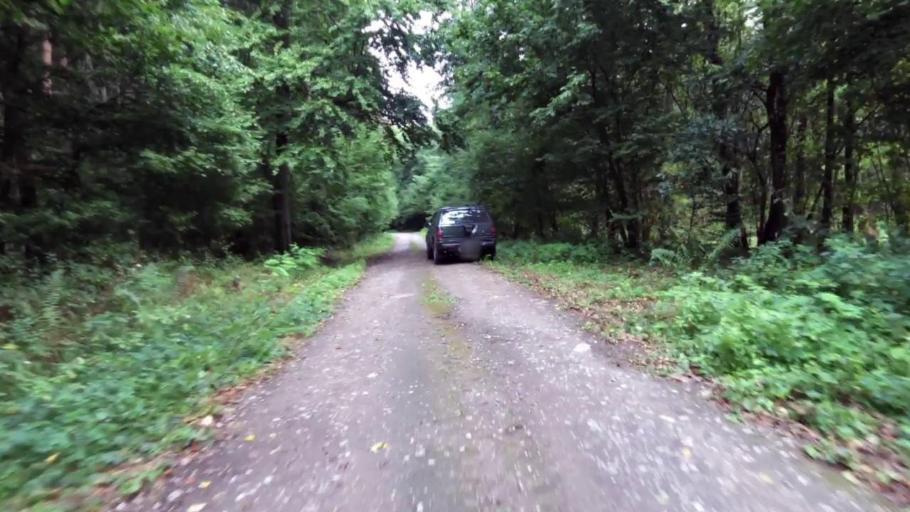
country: PL
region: West Pomeranian Voivodeship
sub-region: Powiat mysliborski
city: Debno
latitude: 52.8668
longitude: 14.6949
